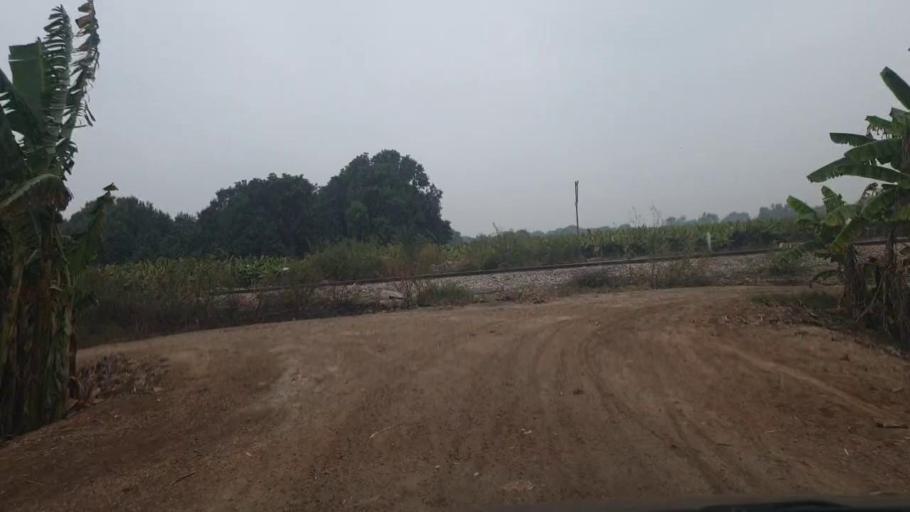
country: PK
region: Sindh
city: Tando Adam
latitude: 25.8028
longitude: 68.6637
